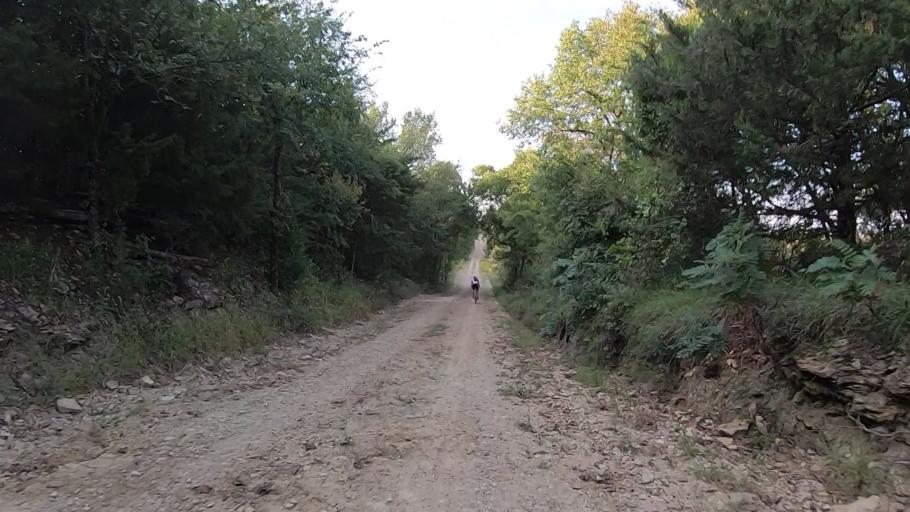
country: US
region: Kansas
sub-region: Marshall County
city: Blue Rapids
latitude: 39.7556
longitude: -96.7506
